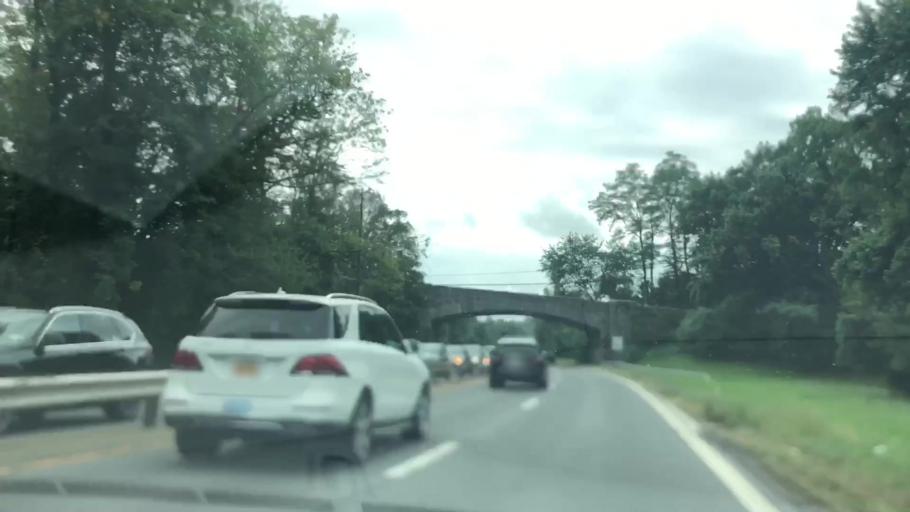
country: US
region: New York
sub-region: Westchester County
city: Hastings-on-Hudson
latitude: 40.9674
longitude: -73.8713
